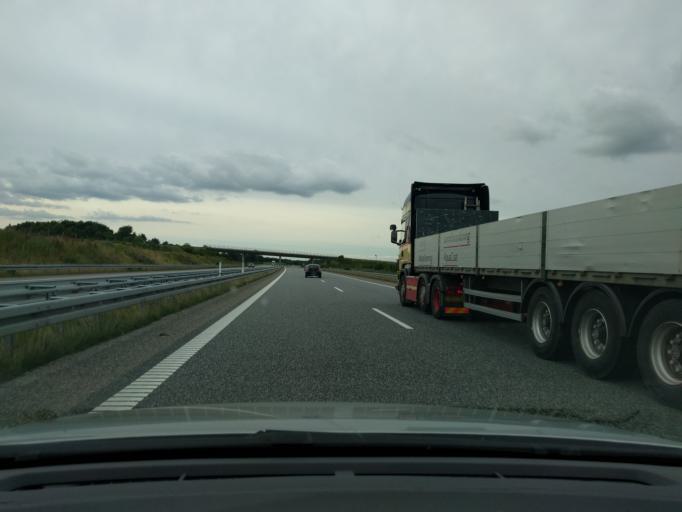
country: DK
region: South Denmark
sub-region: Vejle Kommune
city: Give
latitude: 55.8734
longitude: 9.2438
